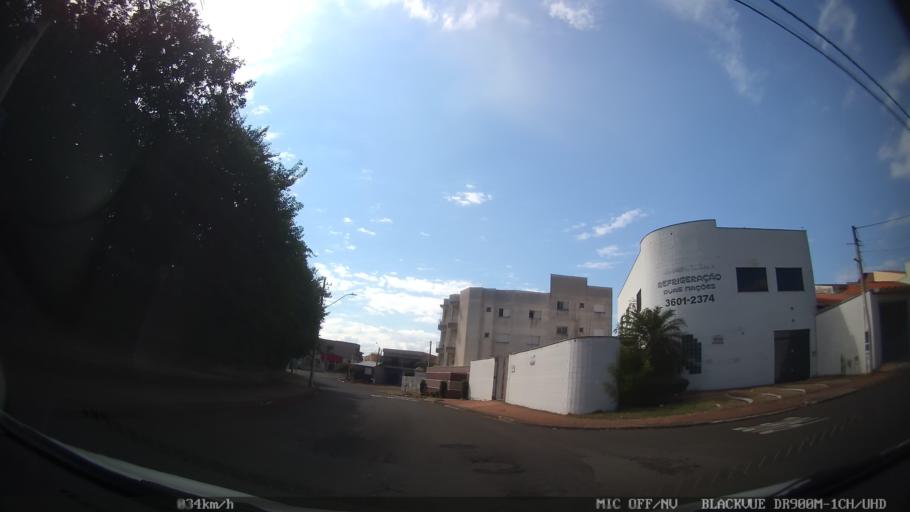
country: BR
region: Sao Paulo
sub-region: Americana
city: Americana
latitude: -22.7150
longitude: -47.3160
